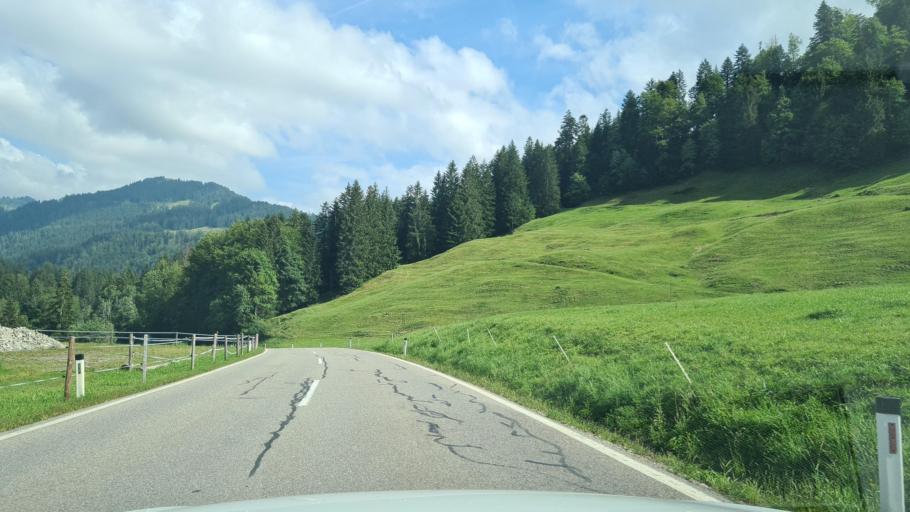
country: AT
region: Vorarlberg
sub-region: Politischer Bezirk Bregenz
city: Sibratsgfall
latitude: 47.4485
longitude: 10.0058
